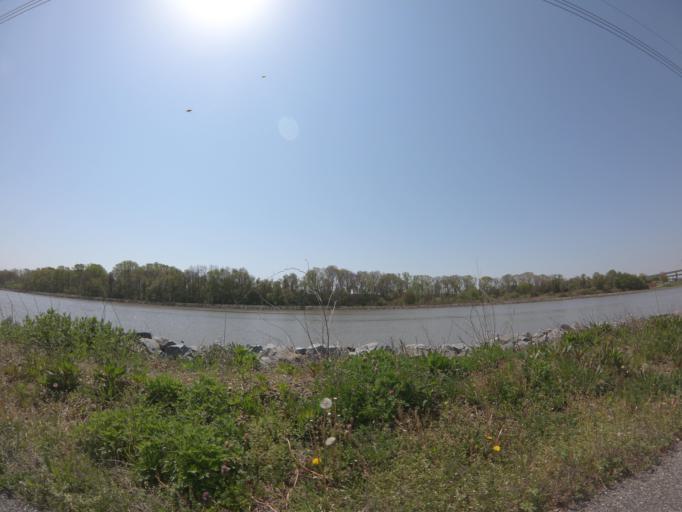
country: US
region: Delaware
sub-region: New Castle County
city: Delaware City
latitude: 39.5572
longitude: -75.6421
